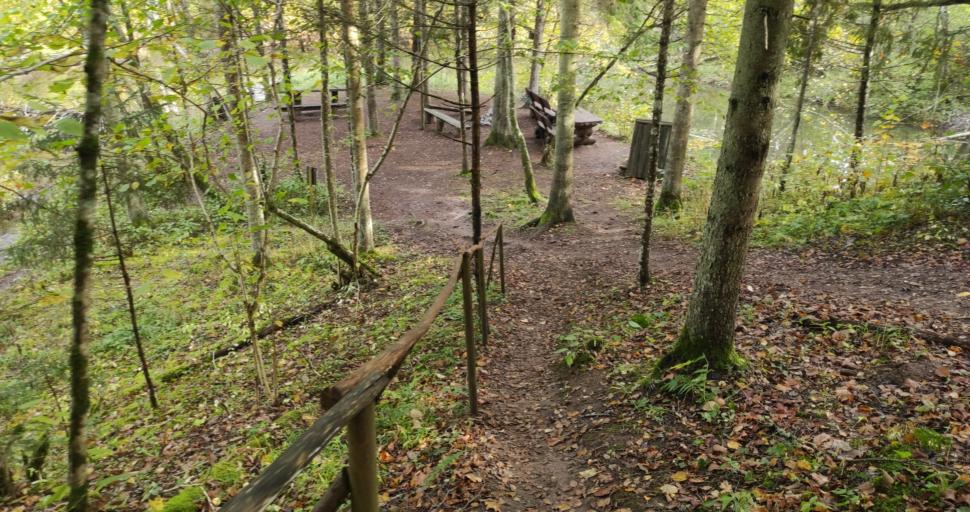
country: LV
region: Jaunpils
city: Jaunpils
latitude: 56.8146
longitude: 22.9566
